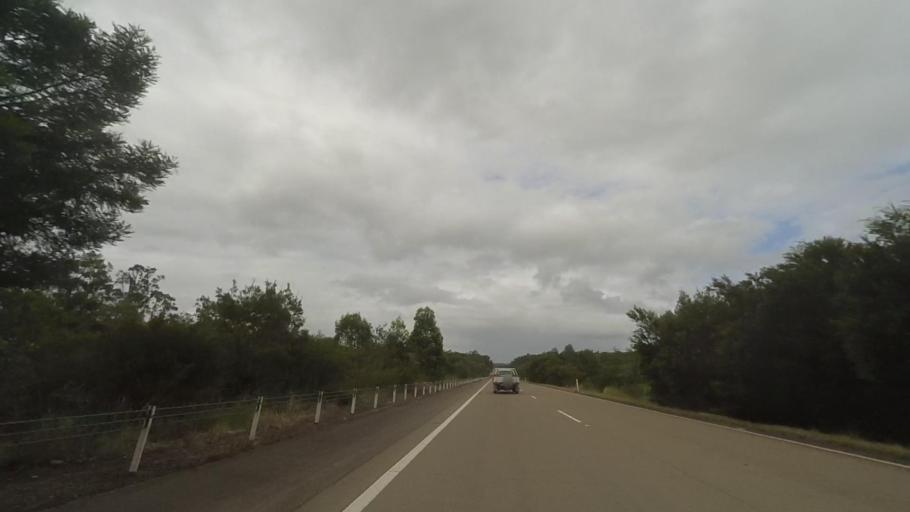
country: AU
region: New South Wales
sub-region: Port Stephens Shire
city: Medowie
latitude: -32.6374
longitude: 151.9335
